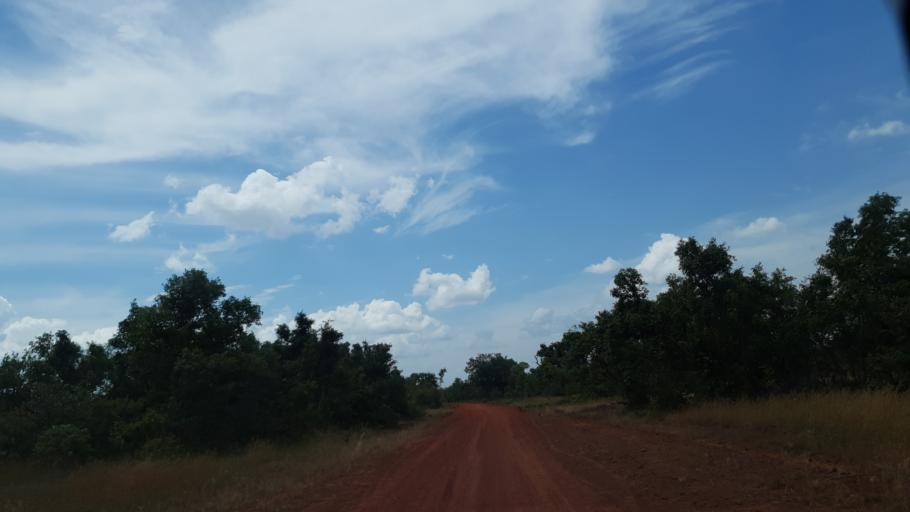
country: ML
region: Sikasso
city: Sikasso
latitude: 11.6861
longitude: -6.2099
